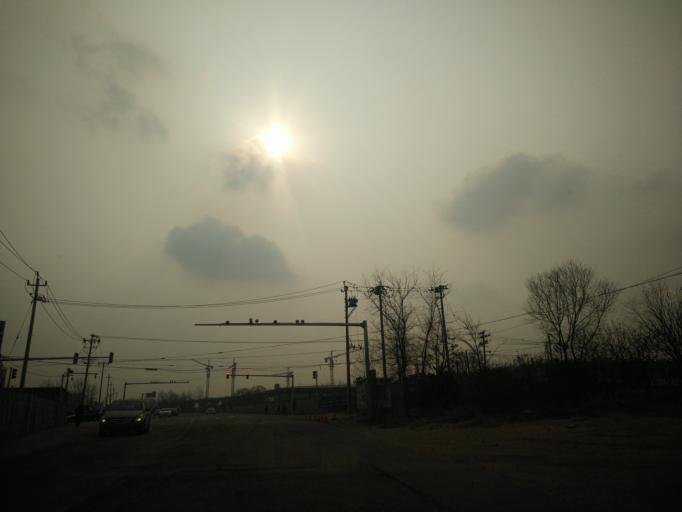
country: CN
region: Beijing
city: Yinghai
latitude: 39.7704
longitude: 116.4406
